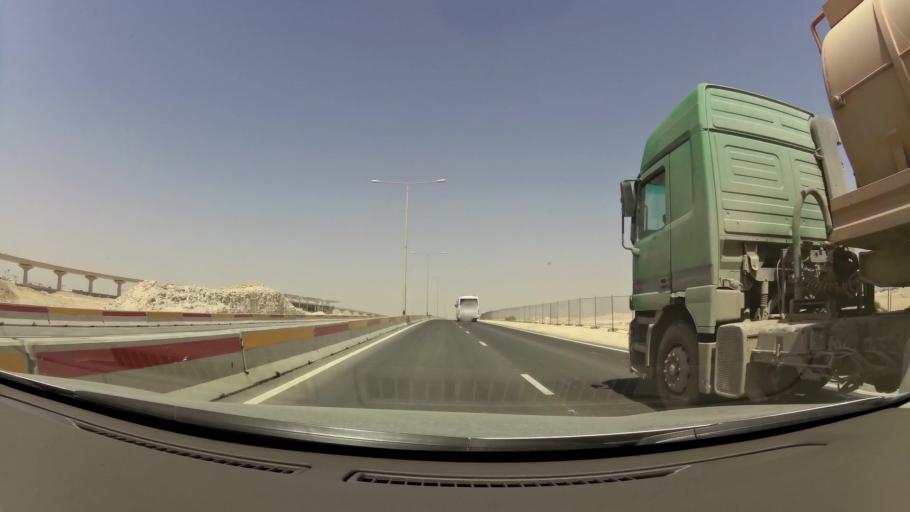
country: QA
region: Baladiyat Umm Salal
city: Umm Salal Muhammad
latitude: 25.3799
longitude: 51.4980
